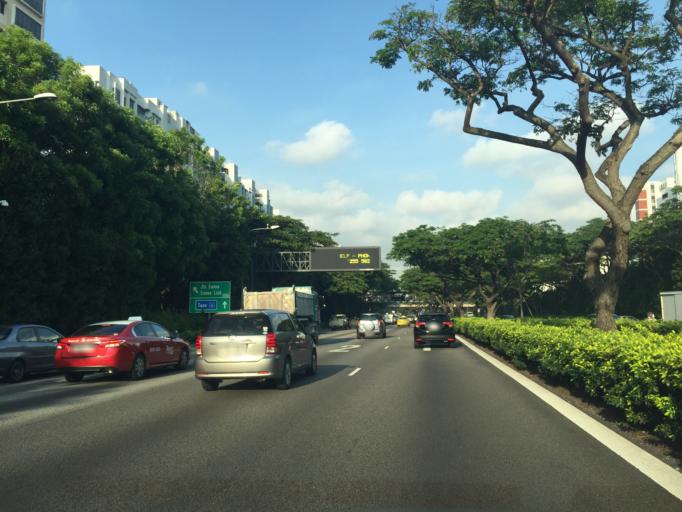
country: SG
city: Singapore
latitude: 1.3293
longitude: 103.9130
